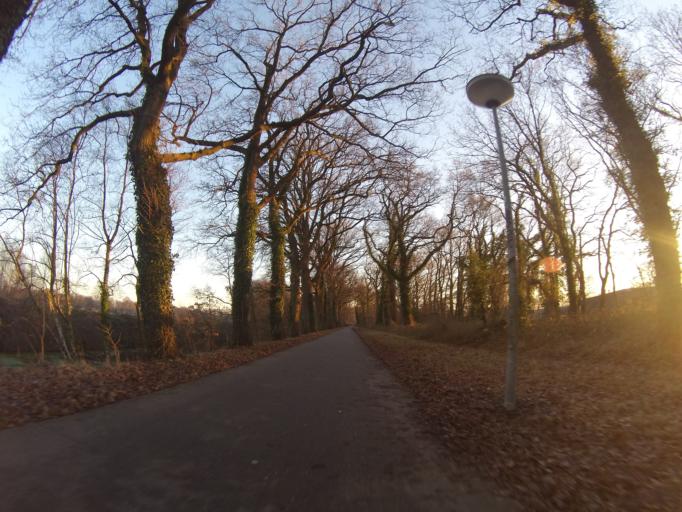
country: NL
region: Drenthe
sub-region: Gemeente Emmen
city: Emmen
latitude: 52.7574
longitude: 6.8933
